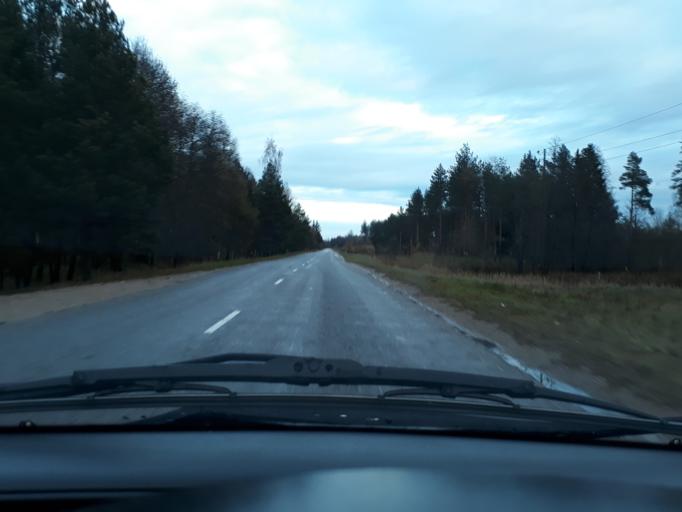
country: LV
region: Dobeles Rajons
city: Dobele
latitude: 56.6040
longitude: 23.2059
